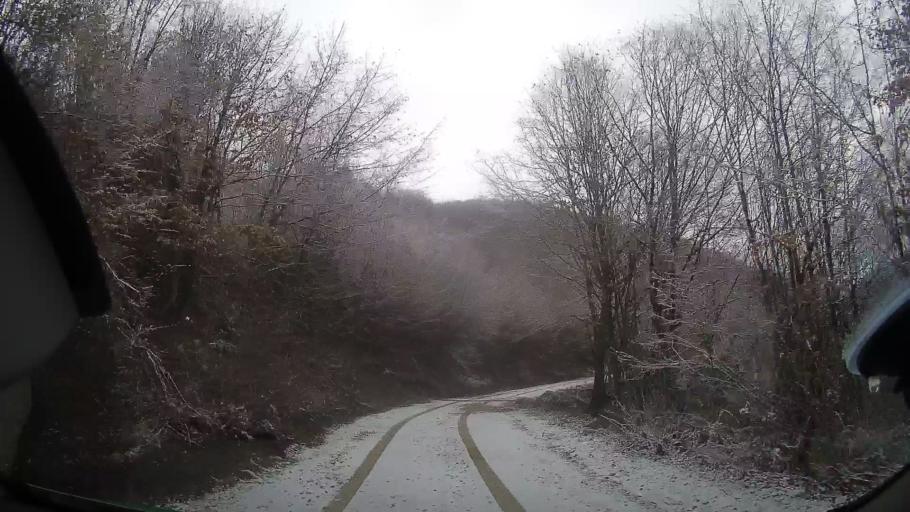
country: RO
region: Cluj
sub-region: Comuna Maguri-Racatau
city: Maguri-Racatau
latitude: 46.6545
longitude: 23.1902
